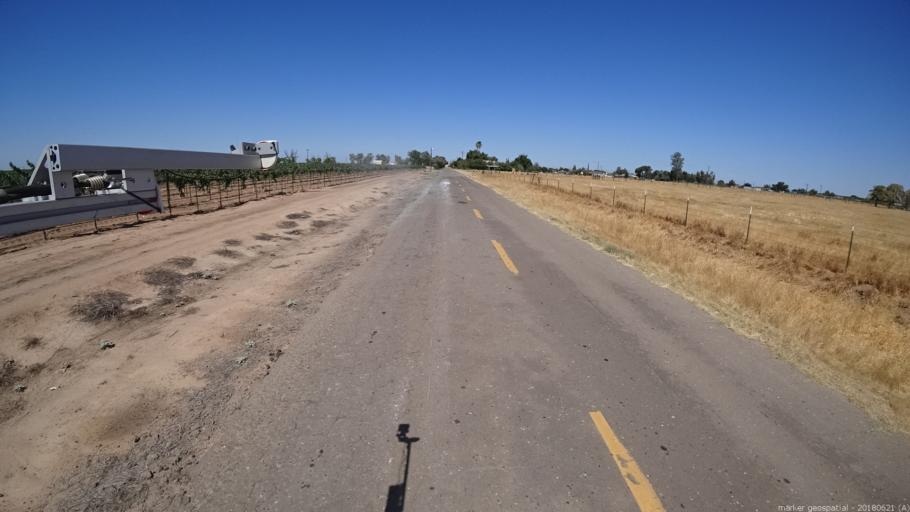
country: US
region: California
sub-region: Madera County
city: Parksdale
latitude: 36.9094
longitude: -119.9539
